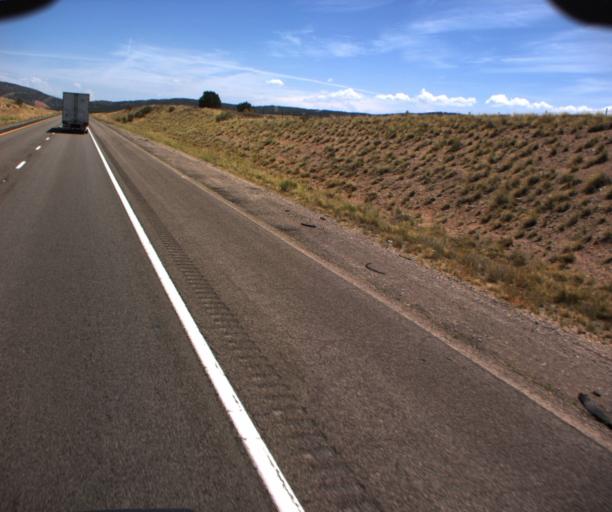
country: US
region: Arizona
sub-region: Mohave County
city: Peach Springs
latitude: 35.2637
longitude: -113.1567
